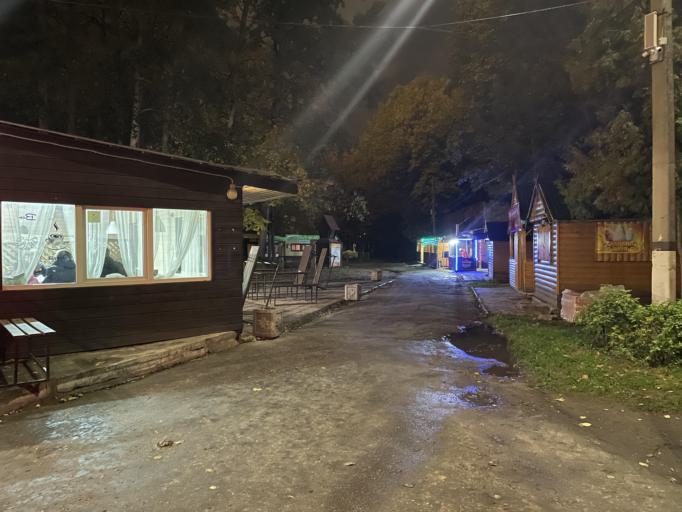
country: RU
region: Chuvashia
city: Novocheboksarsk
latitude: 56.1200
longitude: 47.4772
